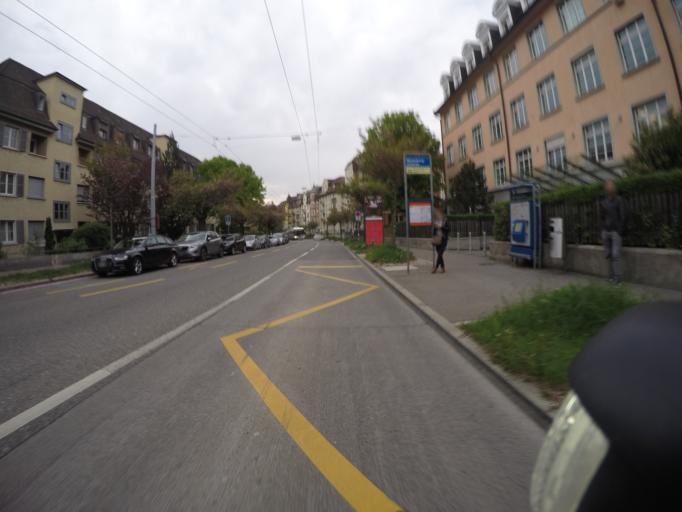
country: CH
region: Zurich
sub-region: Bezirk Zuerich
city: Zuerich (Kreis 6) / Unterstrass
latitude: 47.3926
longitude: 8.5327
